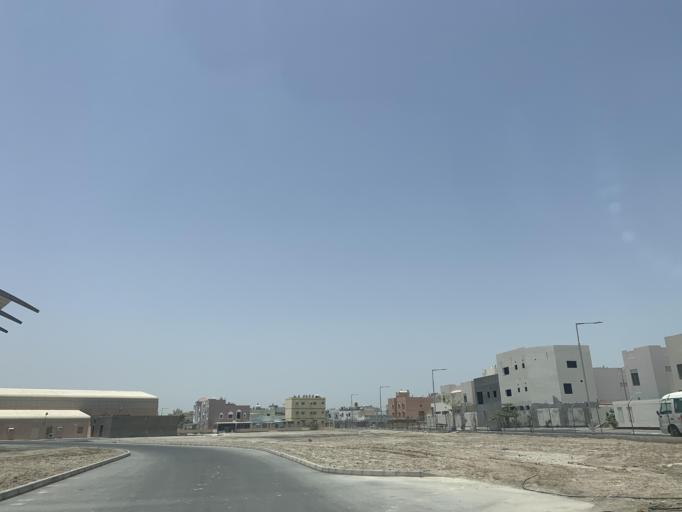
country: BH
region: Northern
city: Sitrah
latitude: 26.1570
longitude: 50.6257
